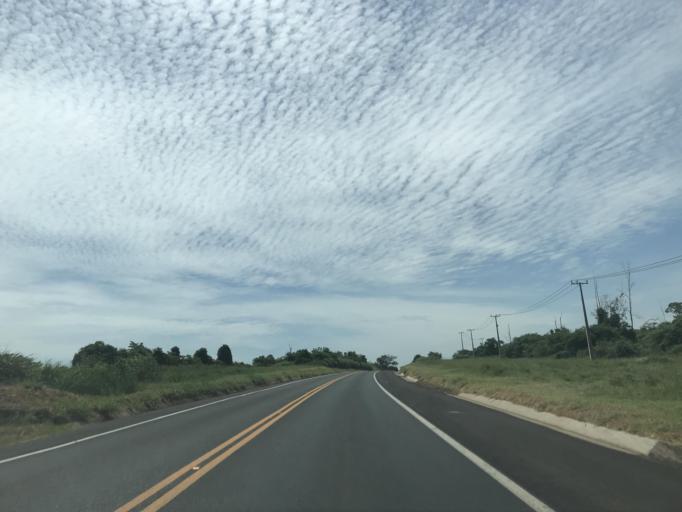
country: BR
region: Parana
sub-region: Paranavai
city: Paranavai
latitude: -23.0146
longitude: -52.5133
